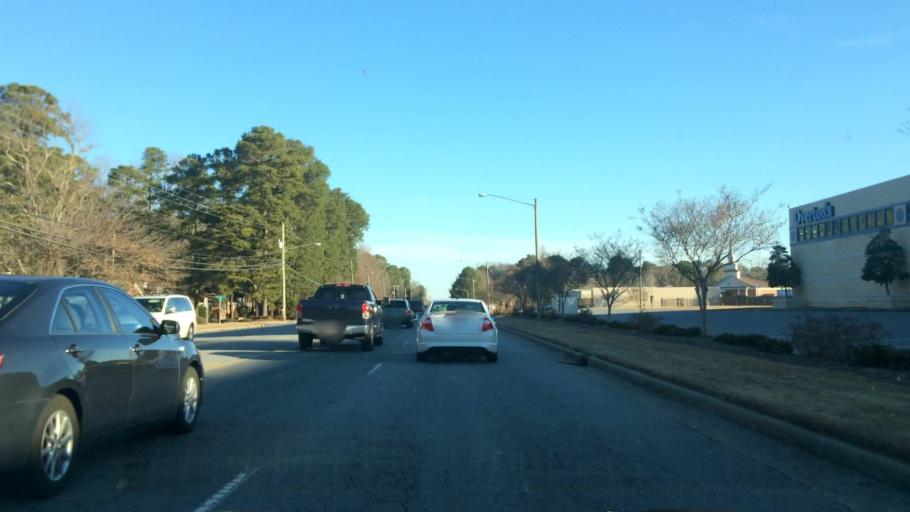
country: US
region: North Carolina
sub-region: Pitt County
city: Summerfield
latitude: 35.5822
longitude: -77.3804
